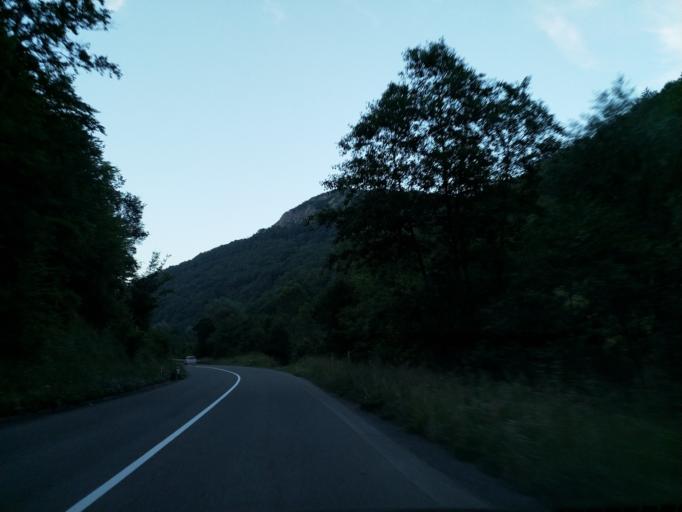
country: RS
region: Central Serbia
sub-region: Rasinski Okrug
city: Aleksandrovac
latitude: 43.3232
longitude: 20.9218
